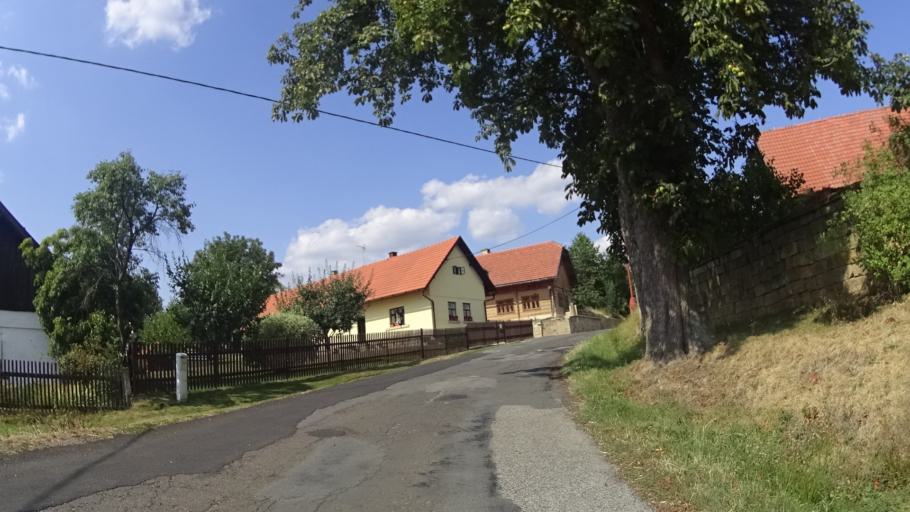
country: CZ
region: Kralovehradecky
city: Liban
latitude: 50.4343
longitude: 15.2558
